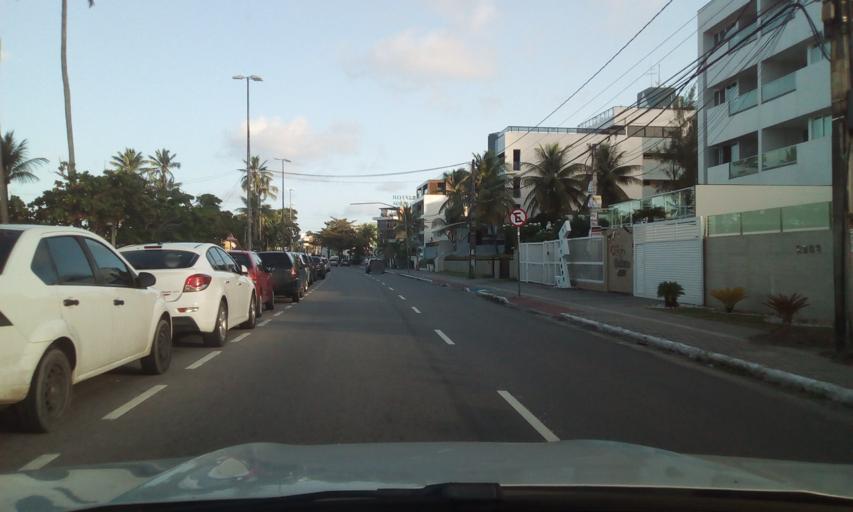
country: BR
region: Paraiba
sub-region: Joao Pessoa
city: Joao Pessoa
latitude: -7.1323
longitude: -34.8216
